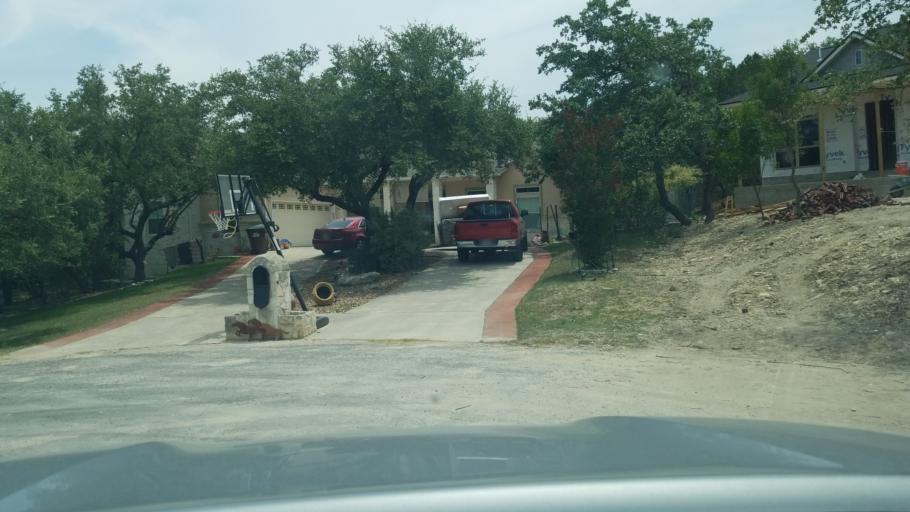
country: US
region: Texas
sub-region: Bexar County
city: Timberwood Park
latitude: 29.6861
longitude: -98.5073
